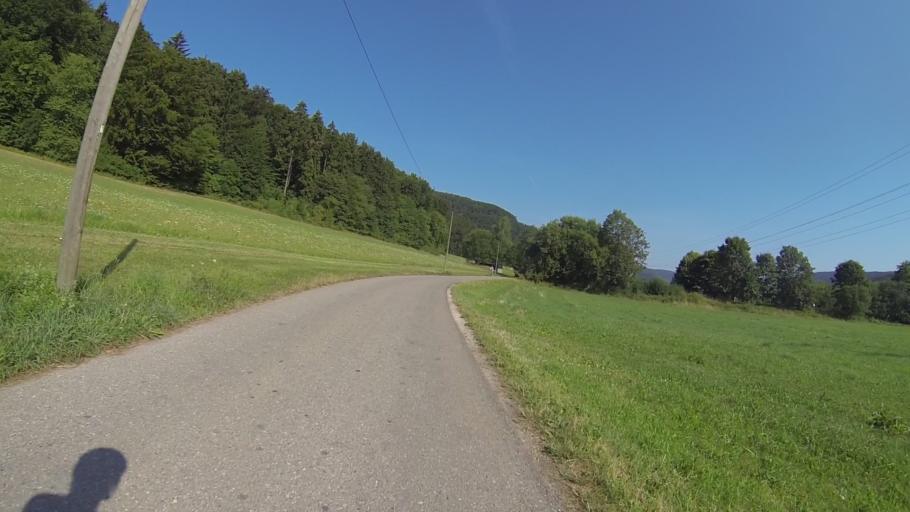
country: DE
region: Baden-Wuerttemberg
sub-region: Regierungsbezirk Stuttgart
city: Konigsbronn
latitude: 48.7475
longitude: 10.0991
